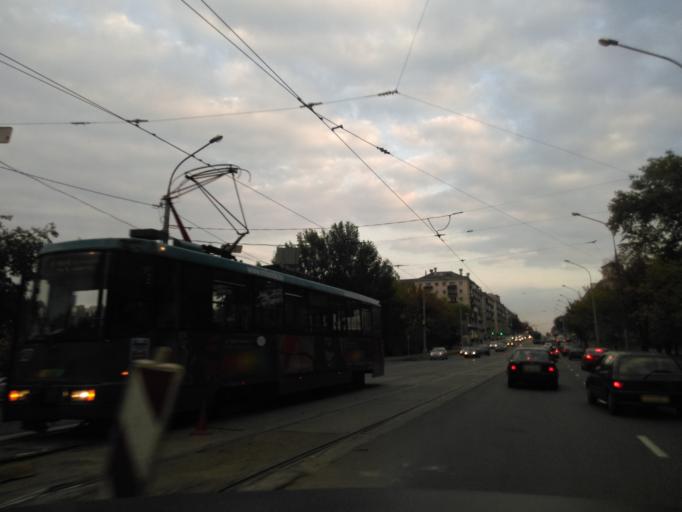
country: BY
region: Minsk
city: Minsk
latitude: 53.9030
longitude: 27.5999
